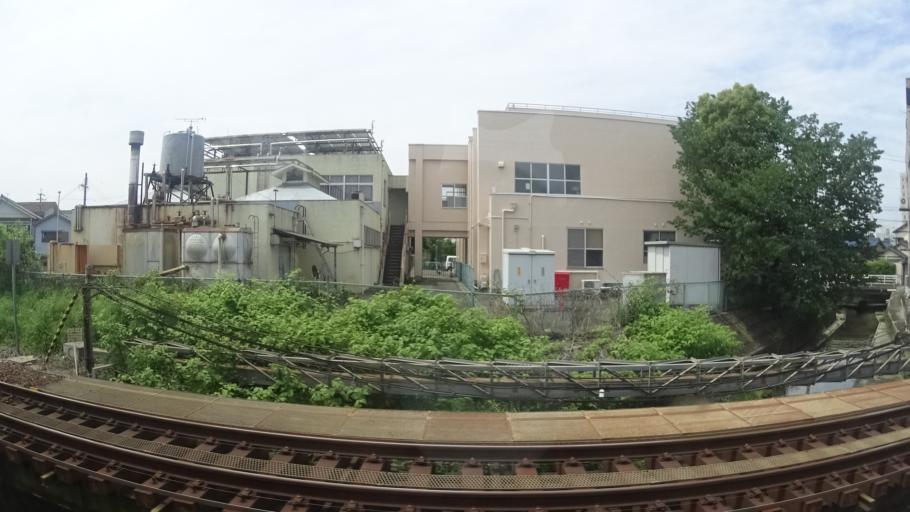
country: JP
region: Mie
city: Hisai-motomachi
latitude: 34.5746
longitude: 136.5380
